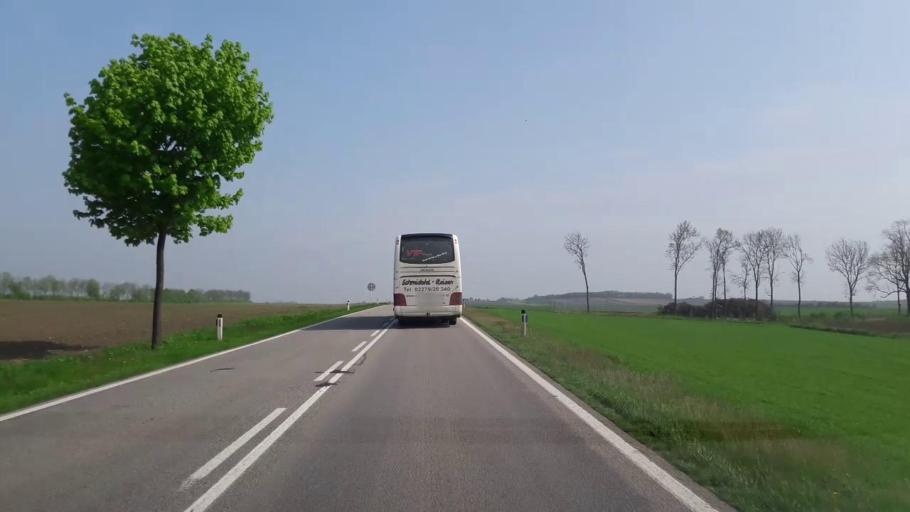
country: AT
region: Lower Austria
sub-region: Politischer Bezirk Hollabrunn
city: Guntersdorf
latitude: 48.6642
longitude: 16.0519
